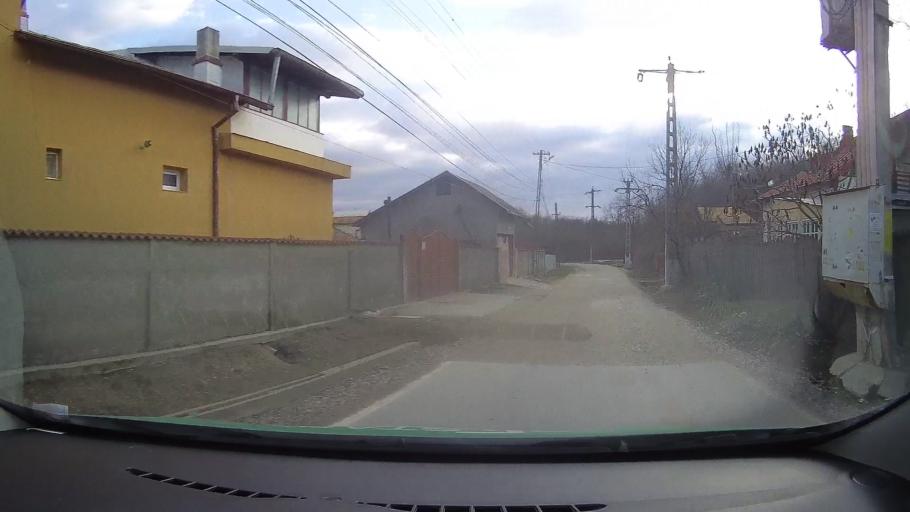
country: RO
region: Dambovita
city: Ion Luca Caragiale
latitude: 44.9136
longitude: 25.6939
